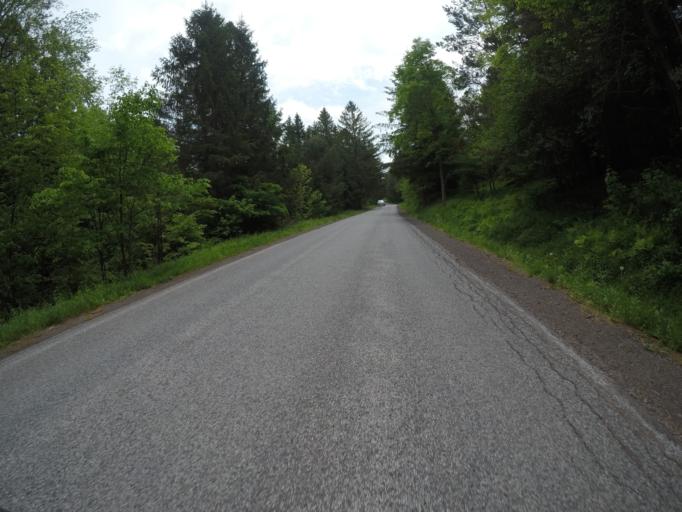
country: US
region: New York
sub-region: Delaware County
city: Stamford
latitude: 42.2650
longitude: -74.7247
